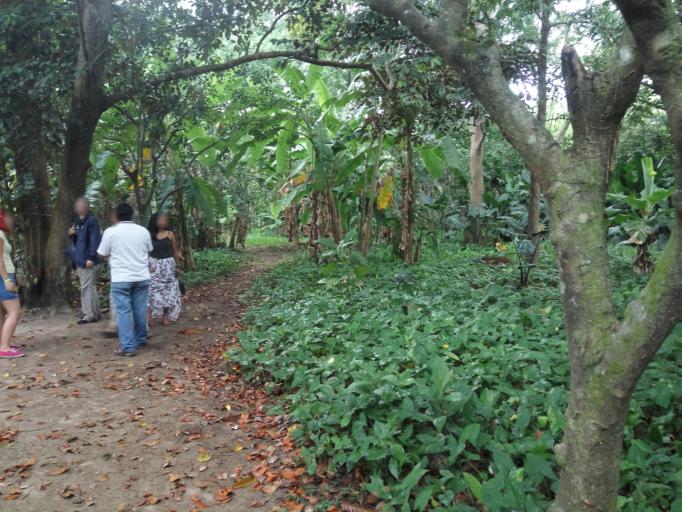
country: MX
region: Tabasco
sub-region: Comalcalco
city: Oriente 2da. Seccion (San Cayetano)
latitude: 18.1830
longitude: -93.2396
